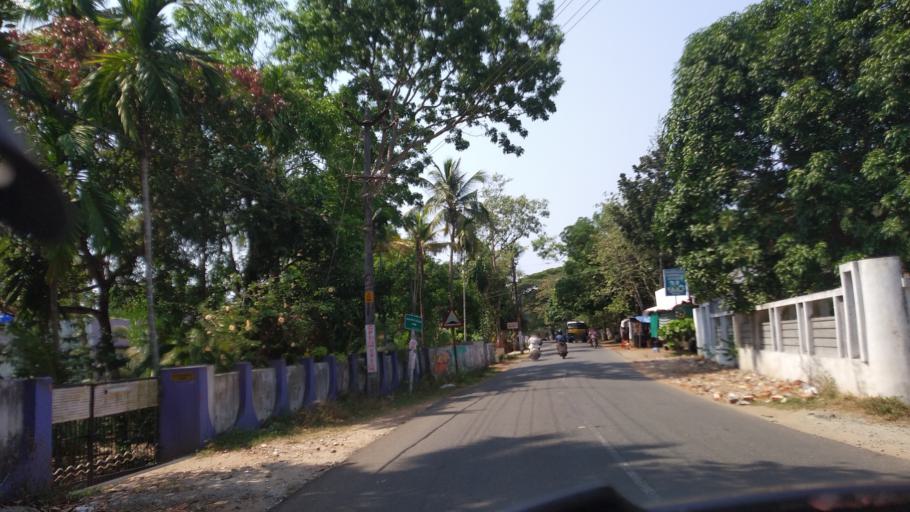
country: IN
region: Kerala
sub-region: Thrissur District
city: Kodungallur
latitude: 10.2391
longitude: 76.1522
